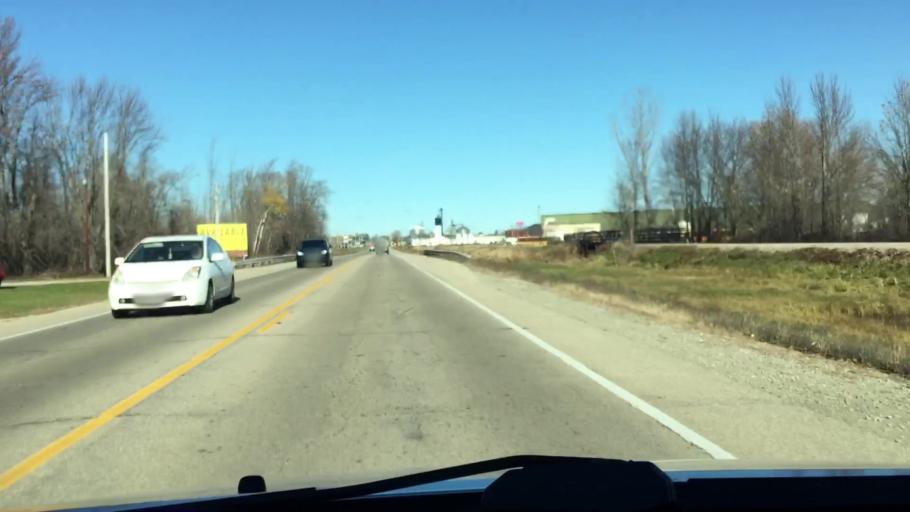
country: US
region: Wisconsin
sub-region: Brown County
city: Pulaski
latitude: 44.6595
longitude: -88.2233
